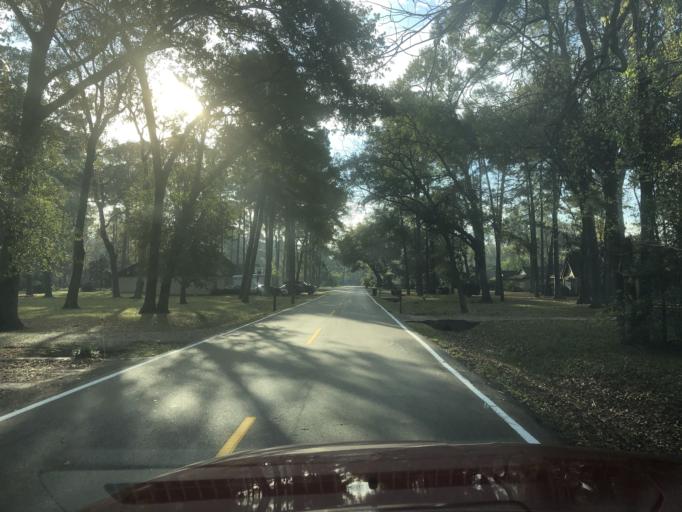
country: US
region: Texas
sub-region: Harris County
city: Spring
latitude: 30.0110
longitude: -95.4751
